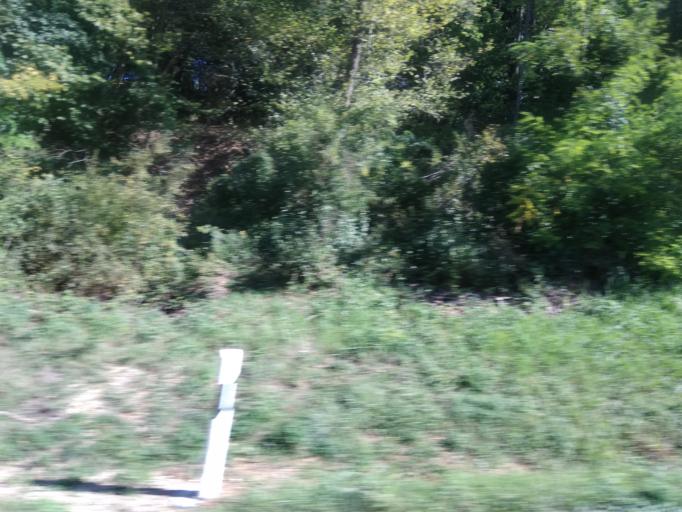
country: DE
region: Baden-Wuerttemberg
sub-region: Karlsruhe Region
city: Billigheim
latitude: 49.3519
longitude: 9.2727
